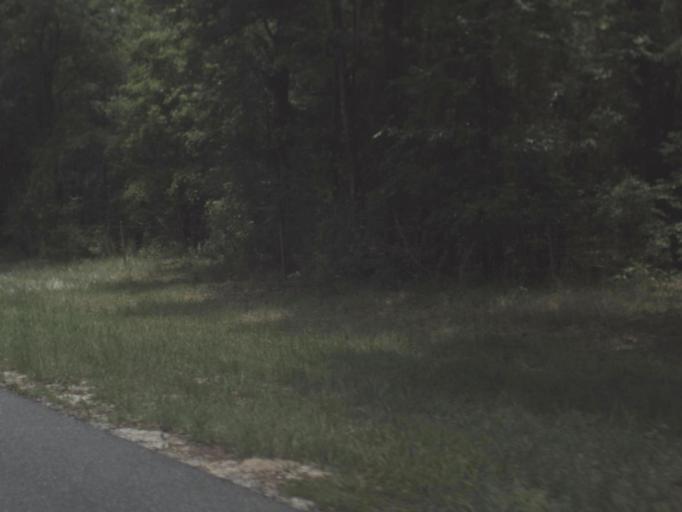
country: US
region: Florida
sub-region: Lafayette County
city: Mayo
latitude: 29.8771
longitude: -82.9564
